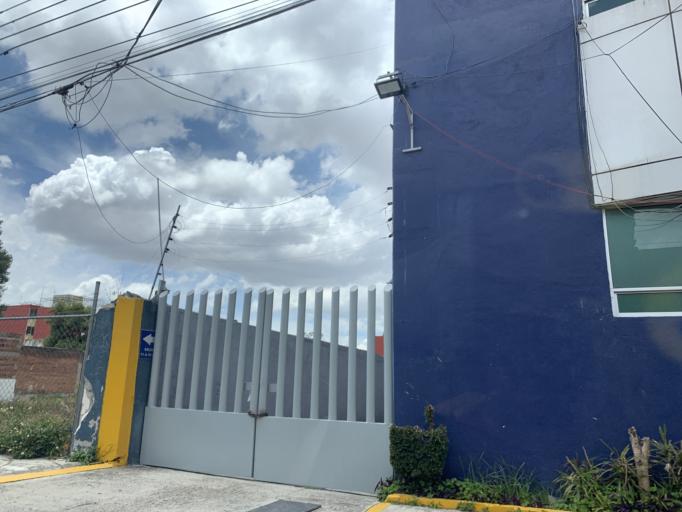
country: MX
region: Puebla
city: Puebla
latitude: 19.0579
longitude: -98.2095
